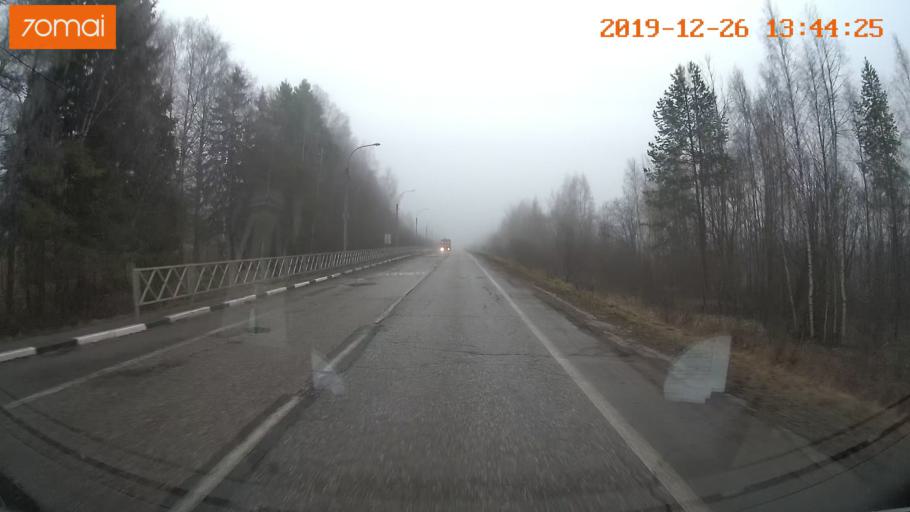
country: RU
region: Vologda
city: Sheksna
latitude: 58.7021
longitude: 38.5062
